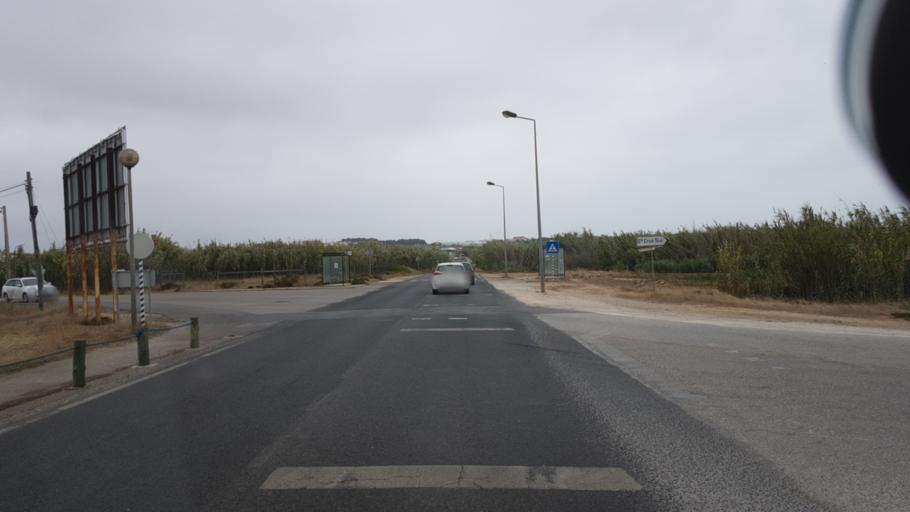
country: PT
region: Lisbon
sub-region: Torres Vedras
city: Silveira
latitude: 39.1268
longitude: -9.3769
